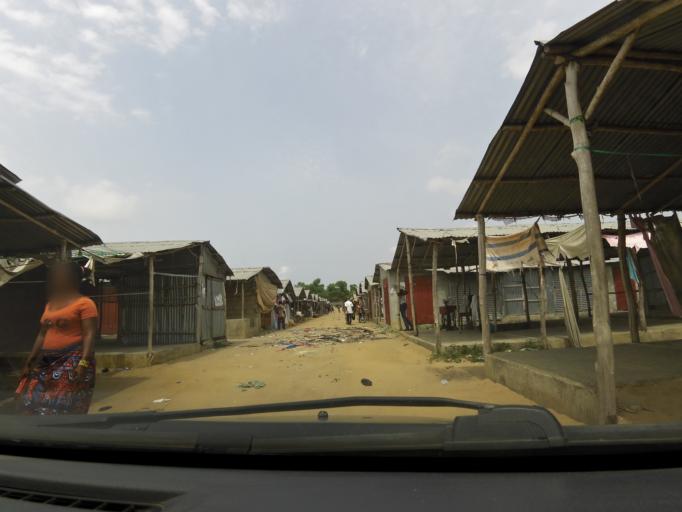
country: BJ
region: Queme
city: Porto-Novo
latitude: 6.3793
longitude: 2.6267
